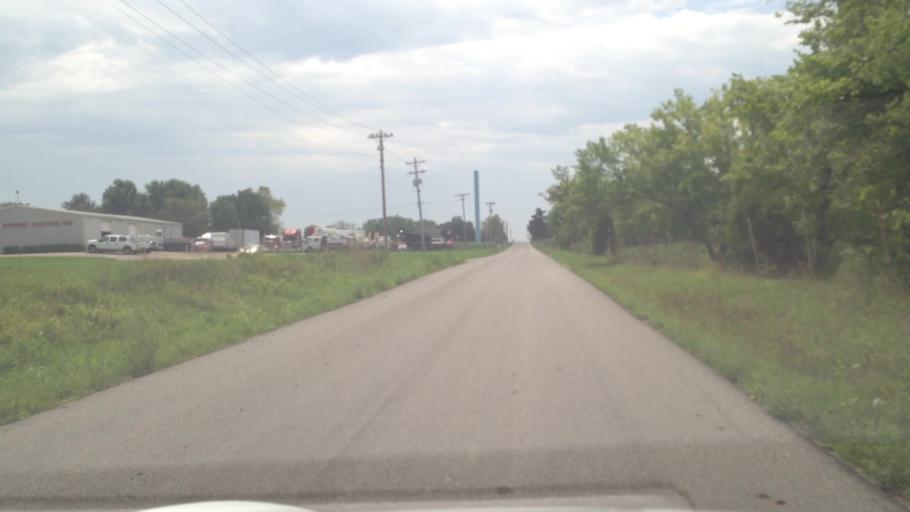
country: US
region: Kansas
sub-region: Crawford County
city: Girard
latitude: 37.5133
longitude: -94.8699
